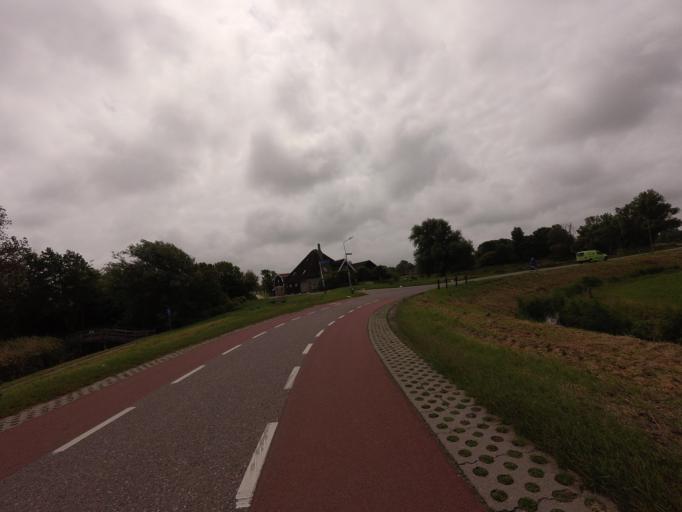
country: NL
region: North Holland
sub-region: Gemeente Schagen
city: Schagen
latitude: 52.7796
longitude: 4.7748
